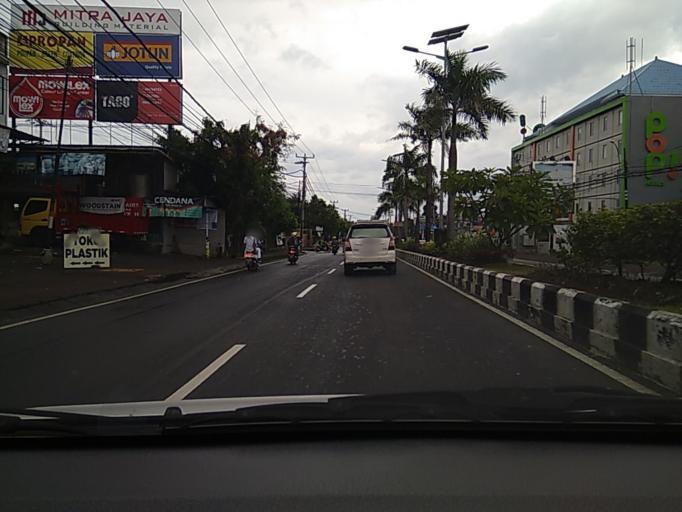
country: ID
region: Bali
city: Bualu
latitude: -8.7852
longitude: 115.1990
